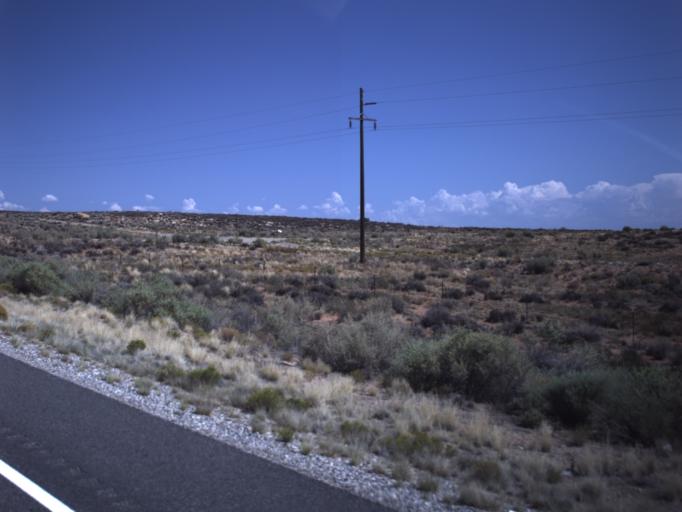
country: US
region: Utah
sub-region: San Juan County
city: Blanding
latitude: 37.3822
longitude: -109.5021
